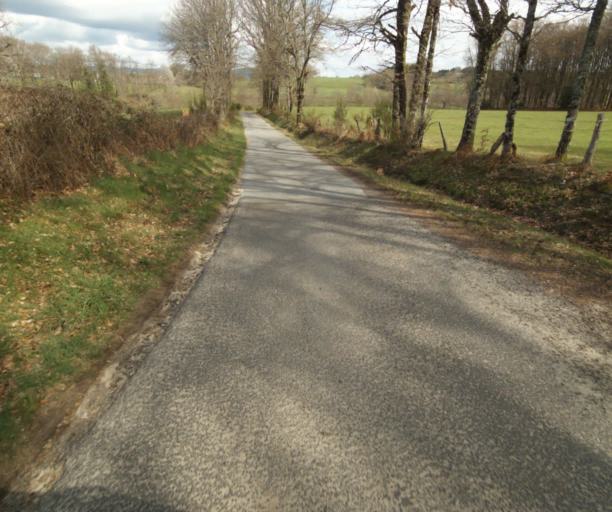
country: FR
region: Limousin
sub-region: Departement de la Correze
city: Correze
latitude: 45.3614
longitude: 1.8986
